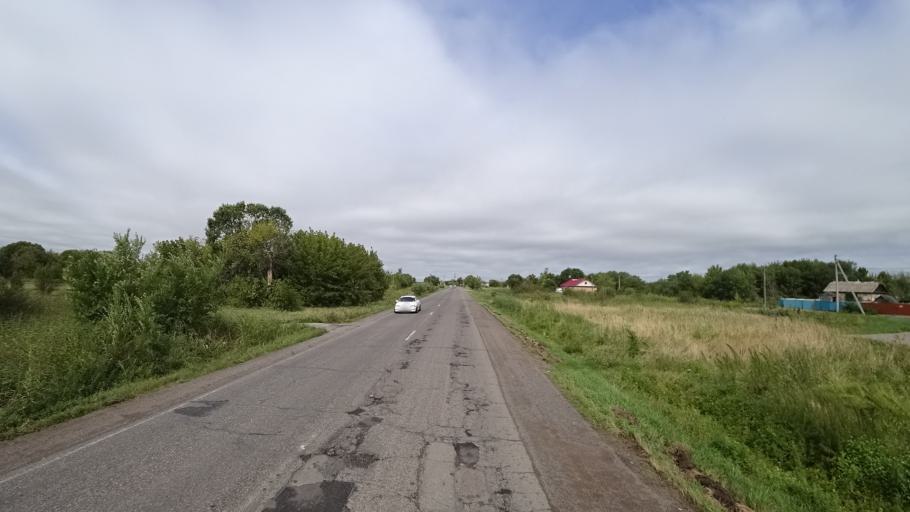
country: RU
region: Primorskiy
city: Monastyrishche
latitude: 44.1930
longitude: 132.4805
